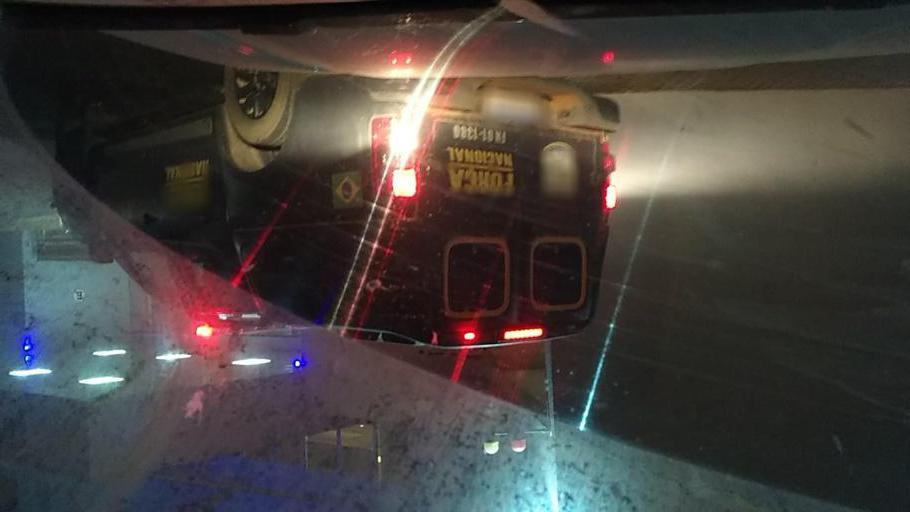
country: BR
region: Rondonia
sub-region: Porto Velho
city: Porto Velho
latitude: -8.7427
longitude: -63.9024
